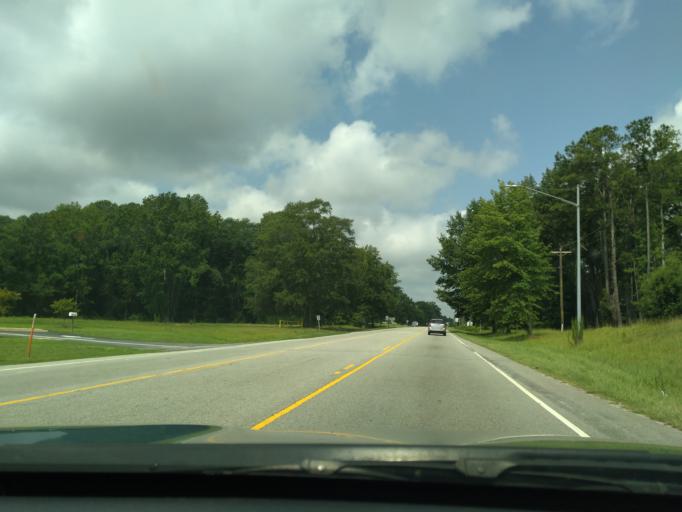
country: US
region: North Carolina
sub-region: Edgecombe County
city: Tarboro
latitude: 35.8934
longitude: -77.5519
